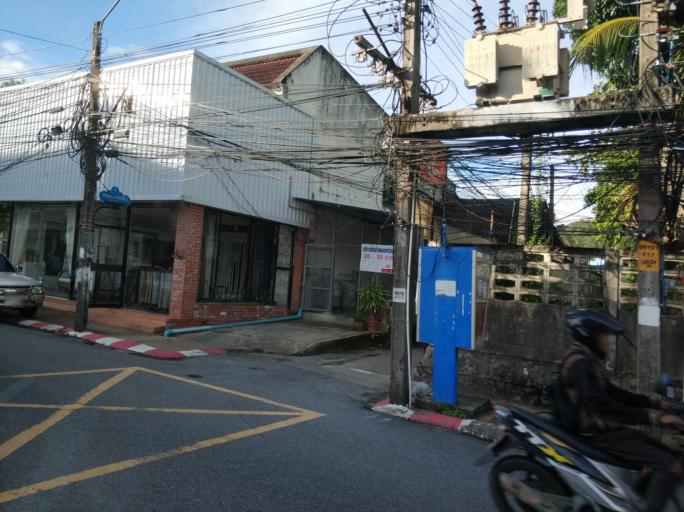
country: TH
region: Phuket
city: Ban Talat Nua
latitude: 7.8855
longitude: 98.3778
